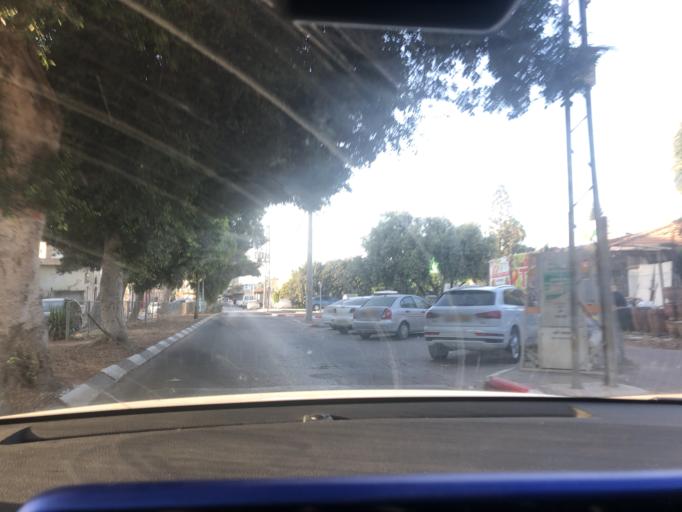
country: IL
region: Central District
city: Lod
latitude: 31.9527
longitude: 34.8973
